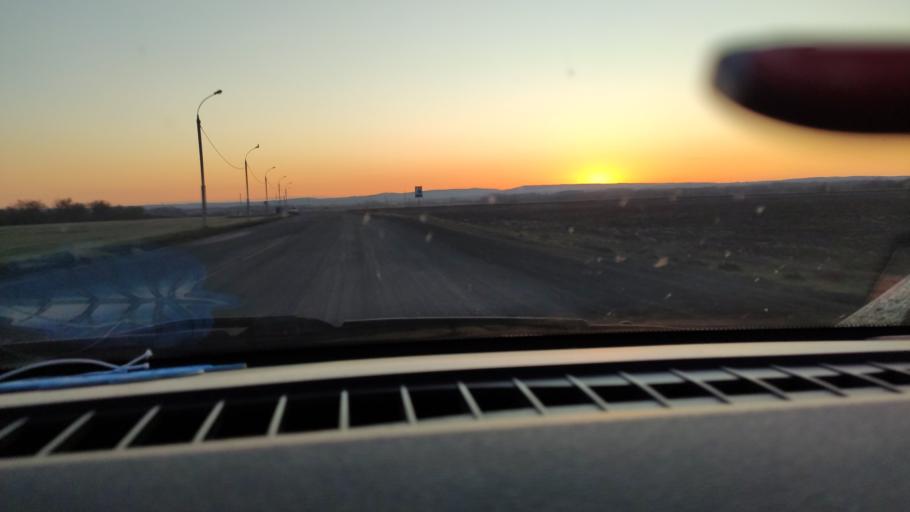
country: RU
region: Saratov
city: Yelshanka
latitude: 51.8123
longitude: 46.2040
